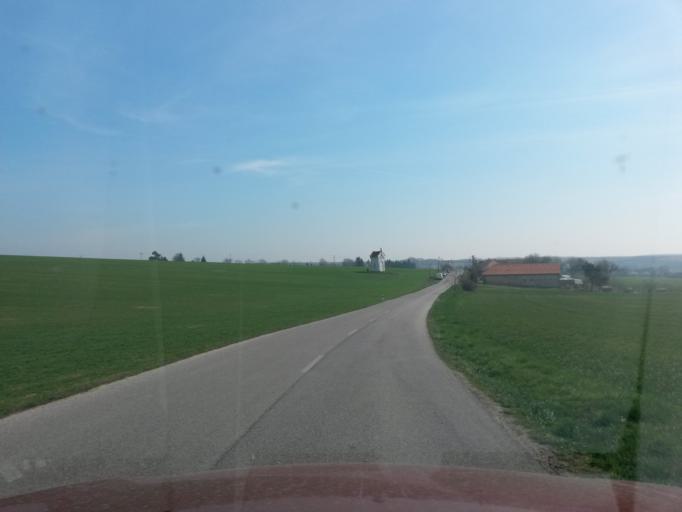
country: SK
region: Nitriansky
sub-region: Okres Nitra
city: Vrable
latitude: 48.1089
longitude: 18.4101
